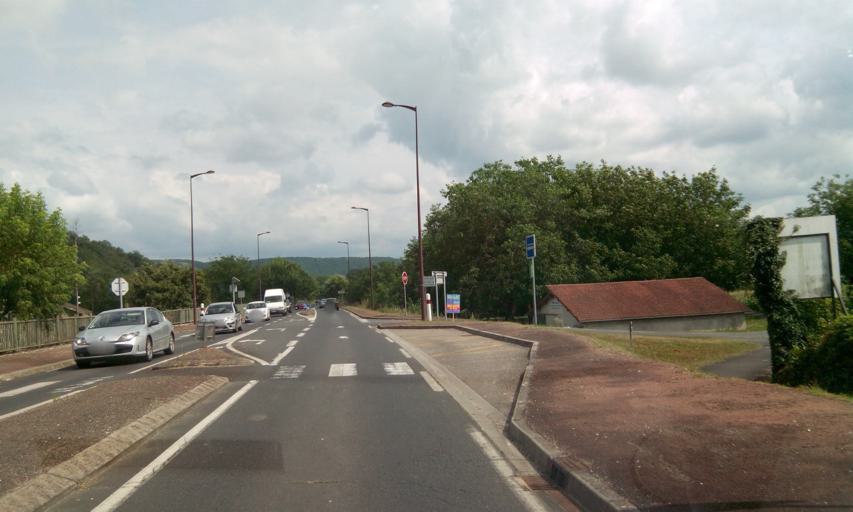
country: FR
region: Midi-Pyrenees
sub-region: Departement du Lot
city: Souillac
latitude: 44.8858
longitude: 1.4082
